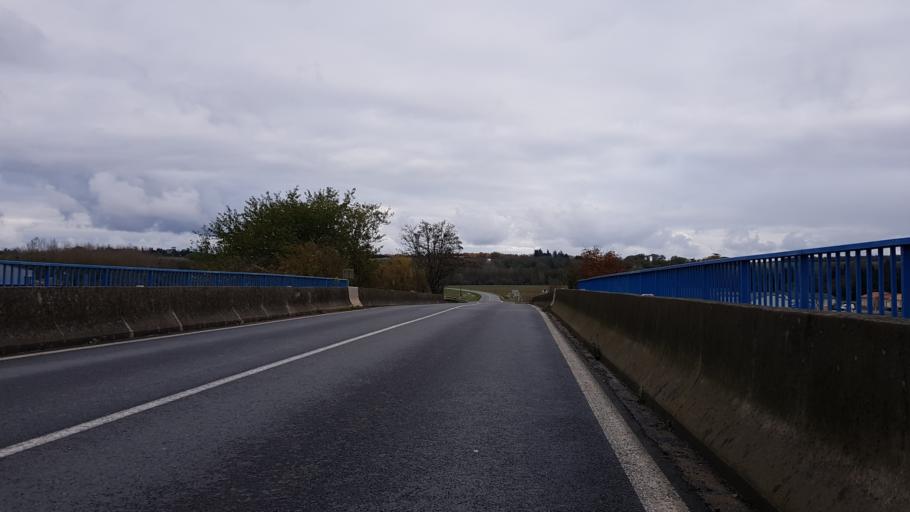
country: FR
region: Poitou-Charentes
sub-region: Departement de la Vienne
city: Chasseneuil-du-Poitou
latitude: 46.6635
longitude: 0.3777
